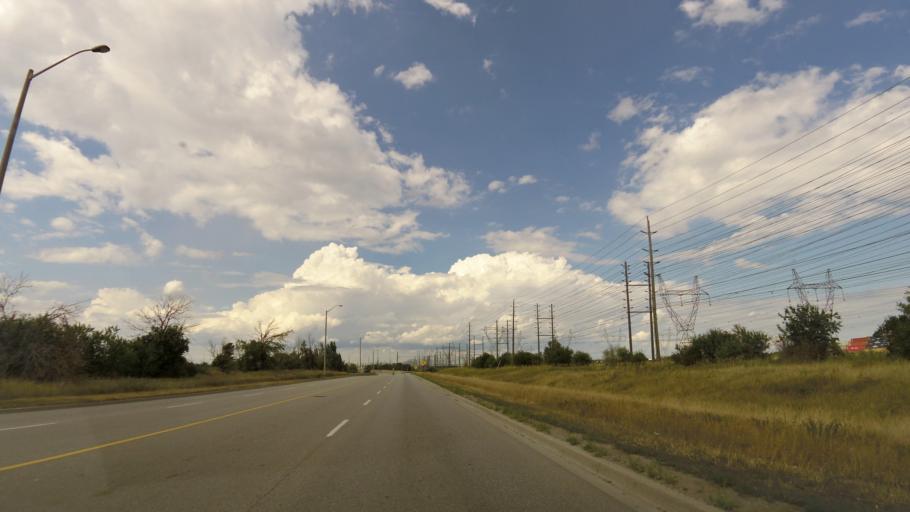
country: CA
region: Ontario
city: Brampton
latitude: 43.6741
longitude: -79.6918
